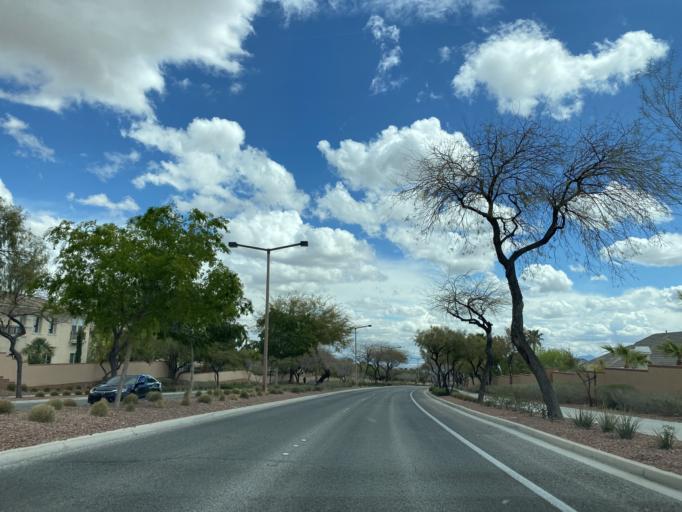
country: US
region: Nevada
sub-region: Clark County
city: Summerlin South
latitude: 36.1848
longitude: -115.3332
